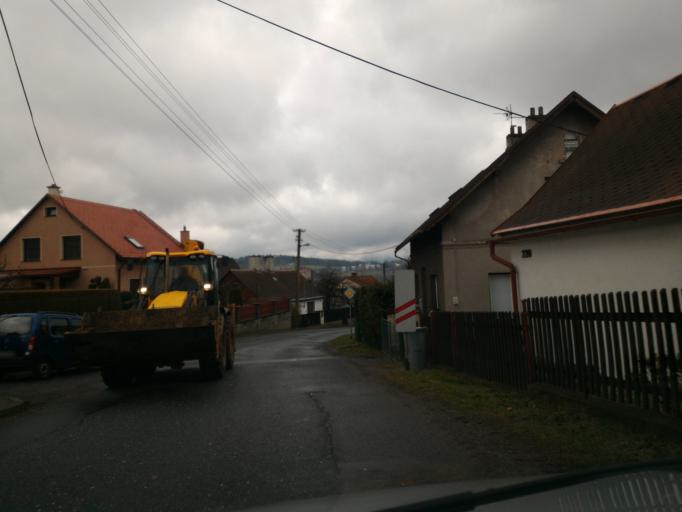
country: CZ
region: Liberecky
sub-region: Okres Liberec
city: Frydlant
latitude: 50.9275
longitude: 15.0723
